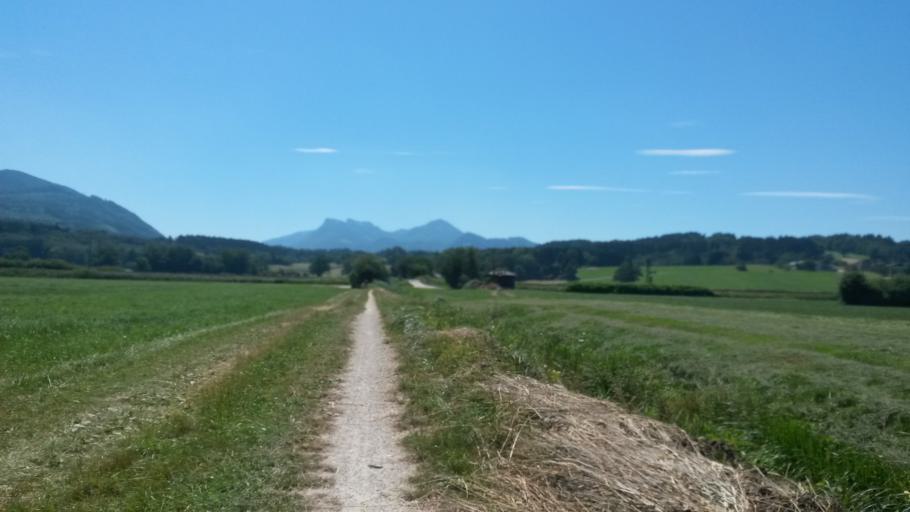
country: DE
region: Bavaria
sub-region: Upper Bavaria
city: Bernau am Chiemsee
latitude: 47.8234
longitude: 12.3699
